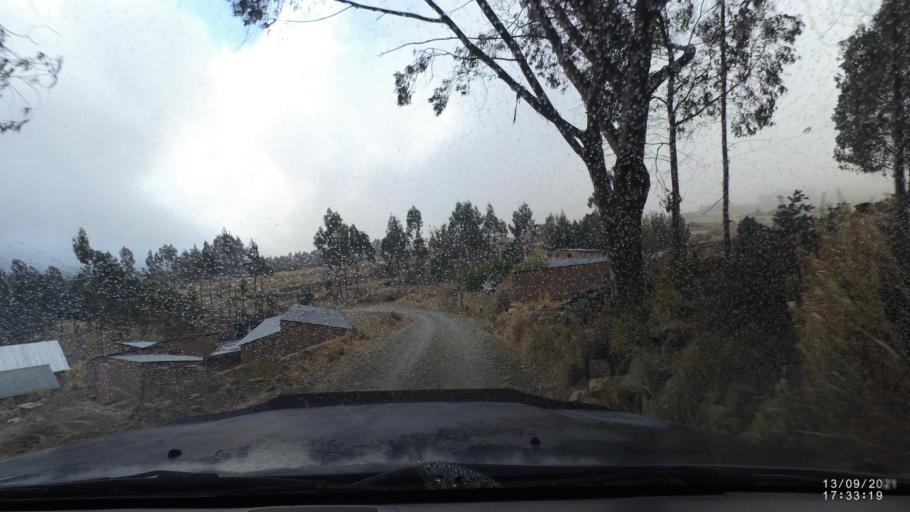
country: BO
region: Cochabamba
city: Colomi
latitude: -17.3677
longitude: -65.7912
